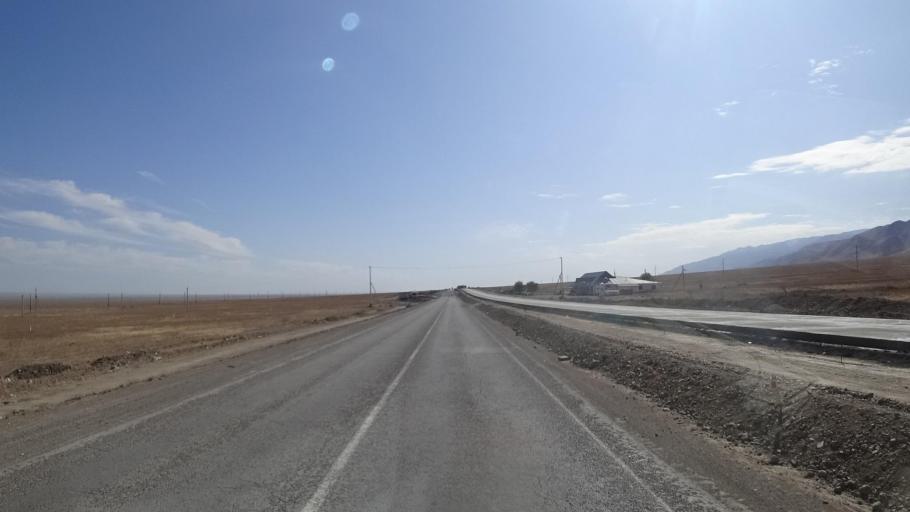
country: KG
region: Chuy
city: Ivanovka
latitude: 43.3852
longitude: 75.1664
